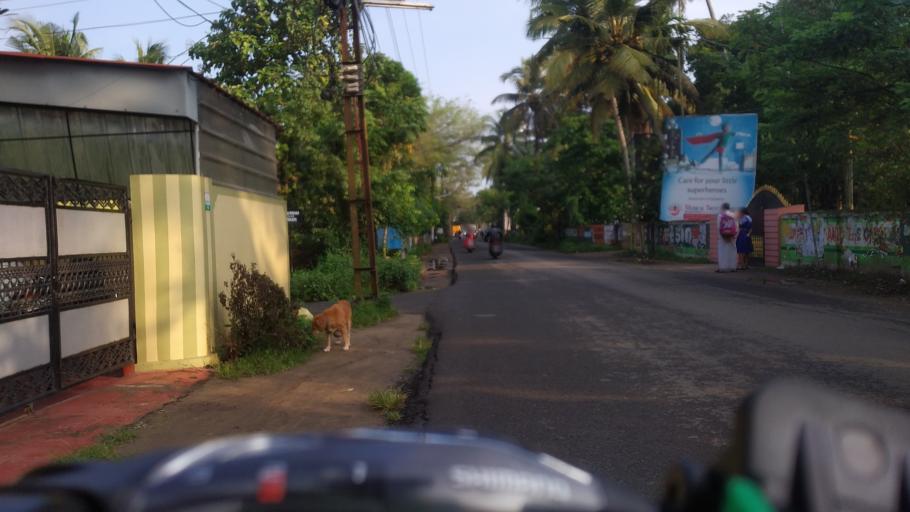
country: IN
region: Kerala
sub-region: Ernakulam
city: Elur
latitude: 10.0697
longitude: 76.2122
